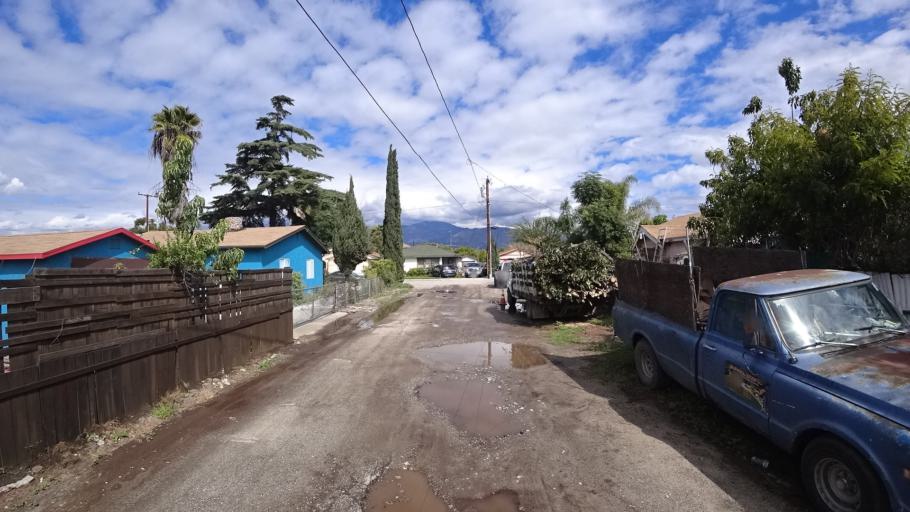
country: US
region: California
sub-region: Los Angeles County
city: Baldwin Park
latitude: 34.0933
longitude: -117.9616
